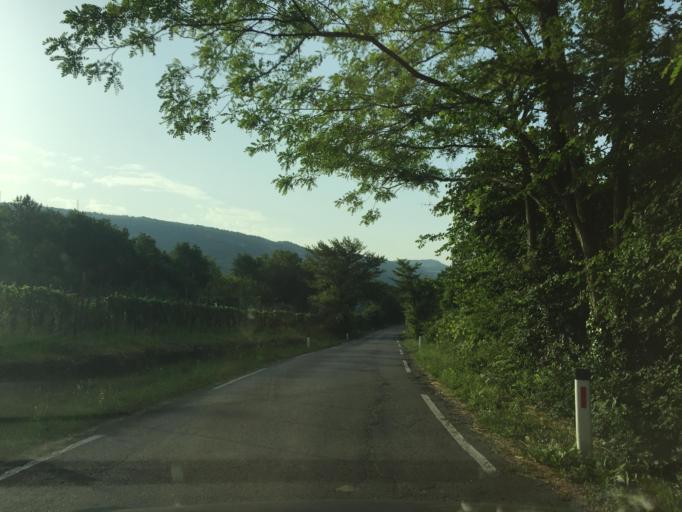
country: IT
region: Friuli Venezia Giulia
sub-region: Provincia di Trieste
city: Dolina
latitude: 45.5810
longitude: 13.8415
